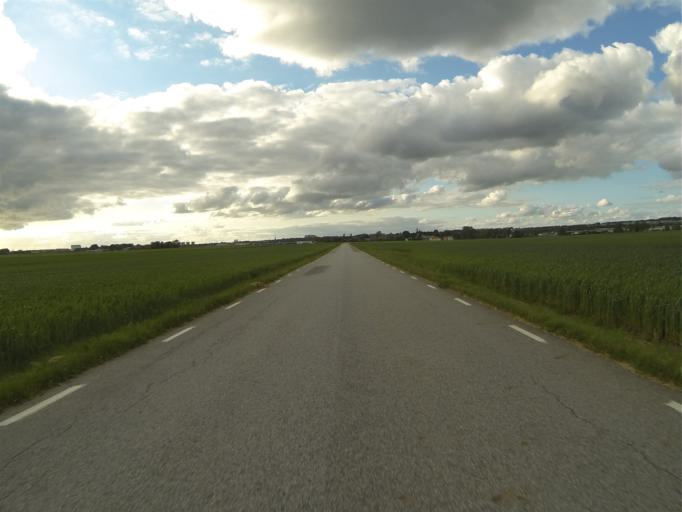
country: SE
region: Skane
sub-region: Staffanstorps Kommun
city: Staffanstorp
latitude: 55.6784
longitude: 13.2277
